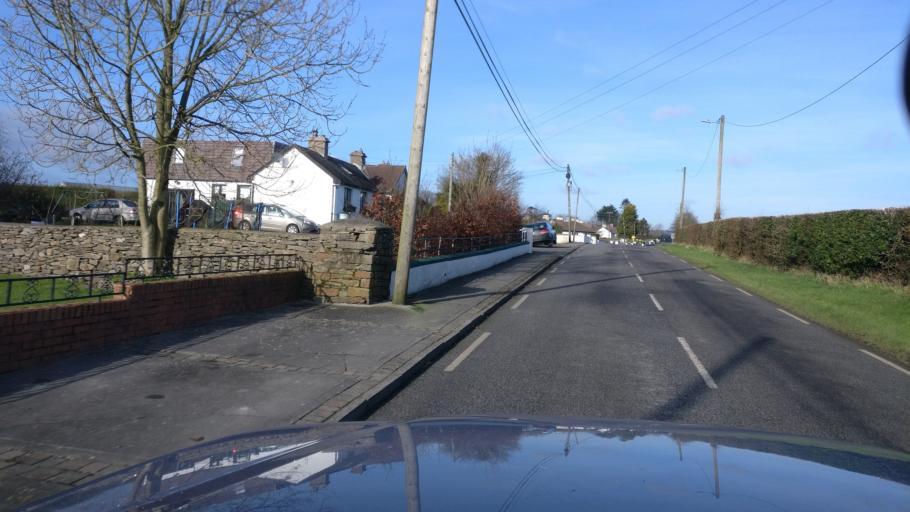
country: IE
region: Leinster
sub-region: Kilkenny
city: Castlecomer
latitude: 52.8682
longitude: -7.1648
